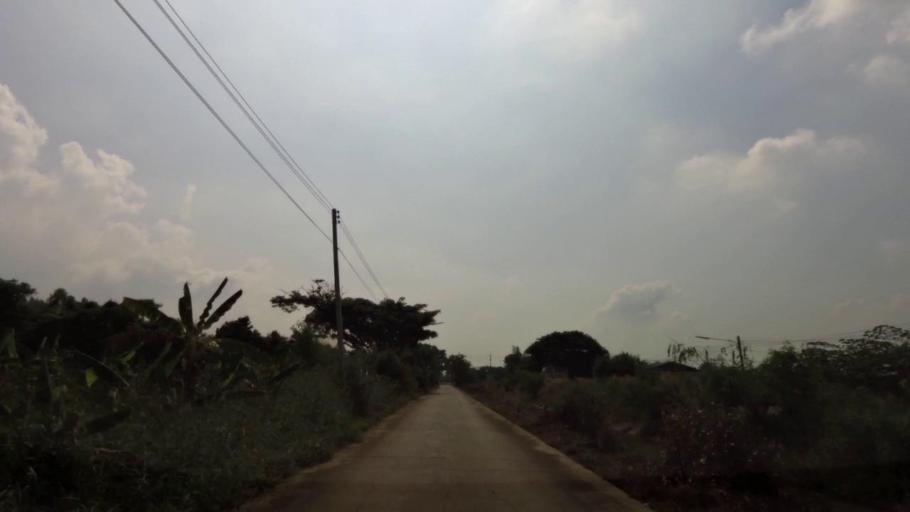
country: TH
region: Ang Thong
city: Wiset Chaichan
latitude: 14.6046
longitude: 100.3940
